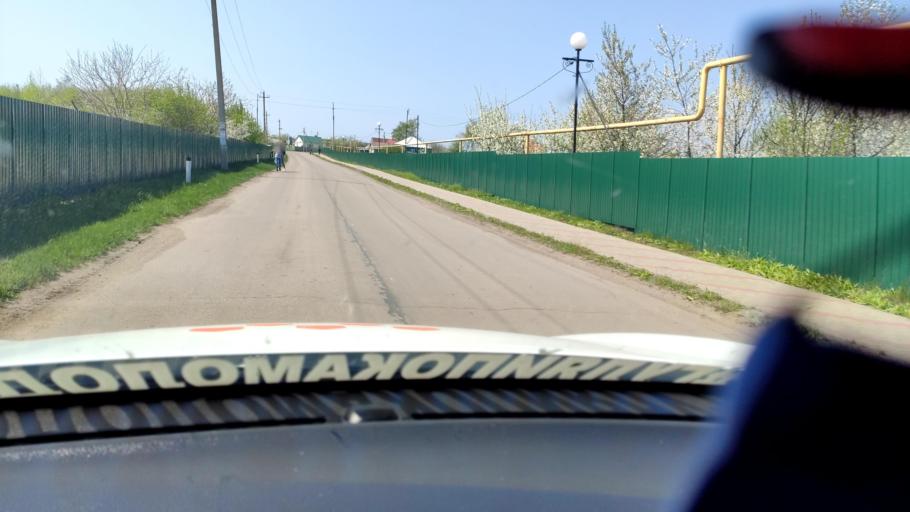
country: RU
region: Voronezj
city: Uryv-Pokrovka
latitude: 51.0763
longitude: 39.1194
